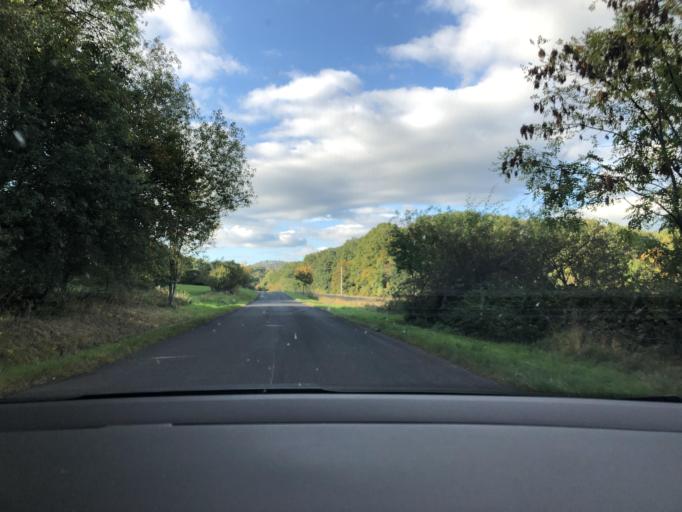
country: CZ
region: Ustecky
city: Zitenice
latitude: 50.5762
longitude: 14.1747
